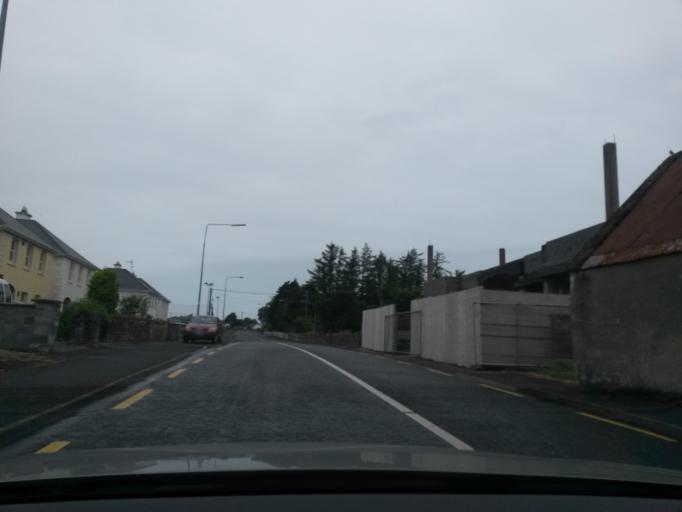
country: IE
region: Connaught
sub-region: Sligo
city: Inishcrone
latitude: 54.2496
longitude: -8.8759
